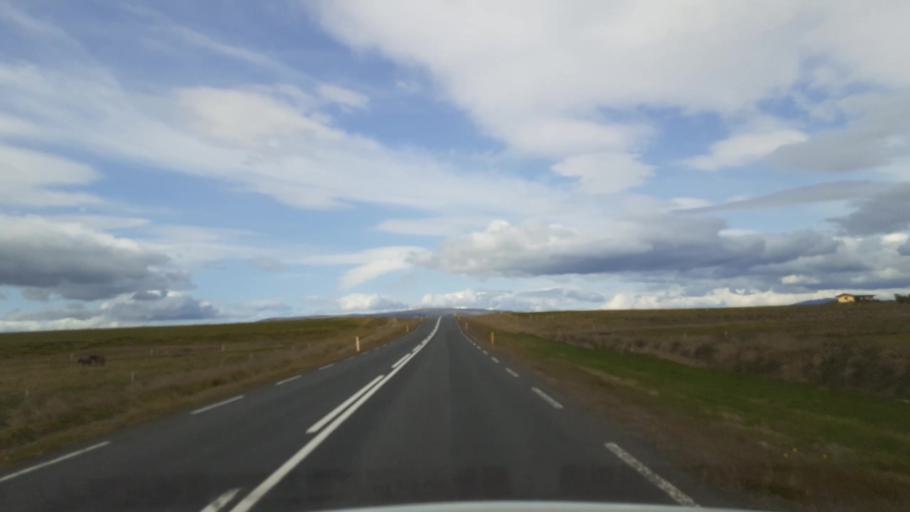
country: IS
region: South
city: Selfoss
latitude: 63.9022
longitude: -20.8104
